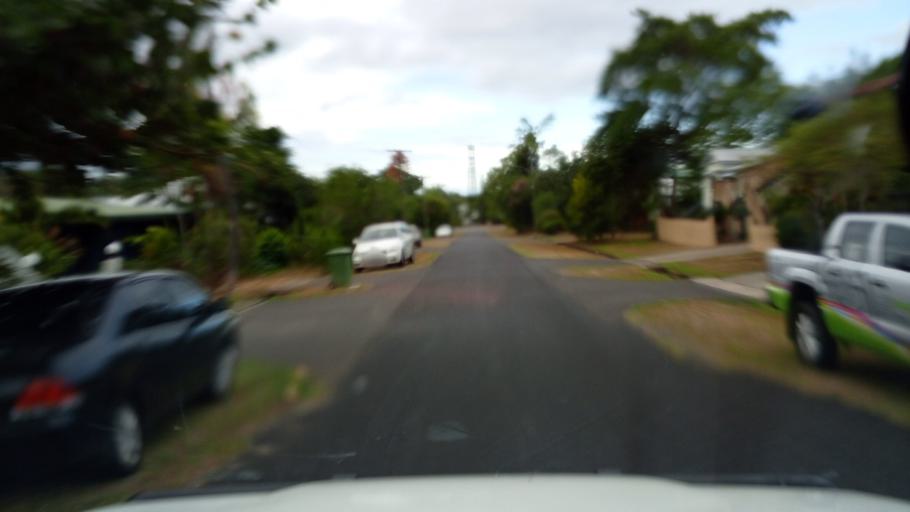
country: AU
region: Queensland
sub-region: Cairns
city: Redlynch
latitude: -16.8801
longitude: 145.7241
